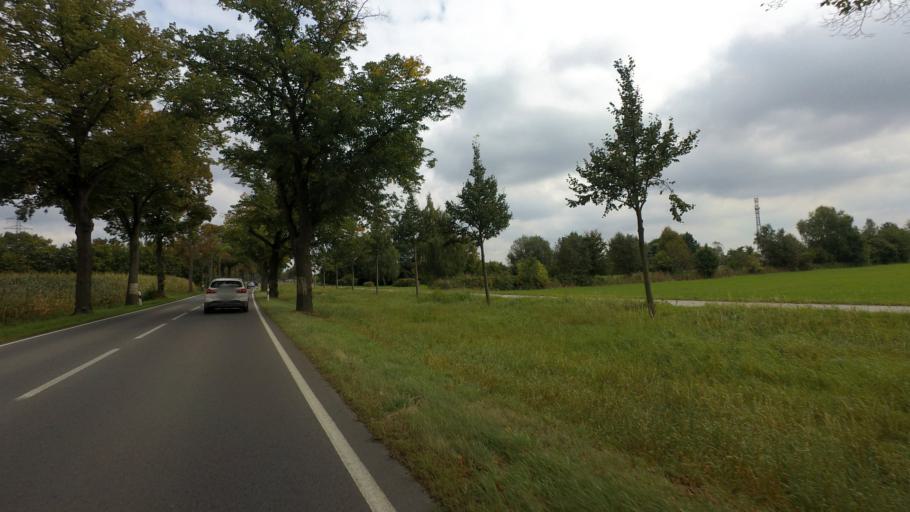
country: DE
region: Brandenburg
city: Finsterwalde
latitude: 51.6376
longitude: 13.7331
